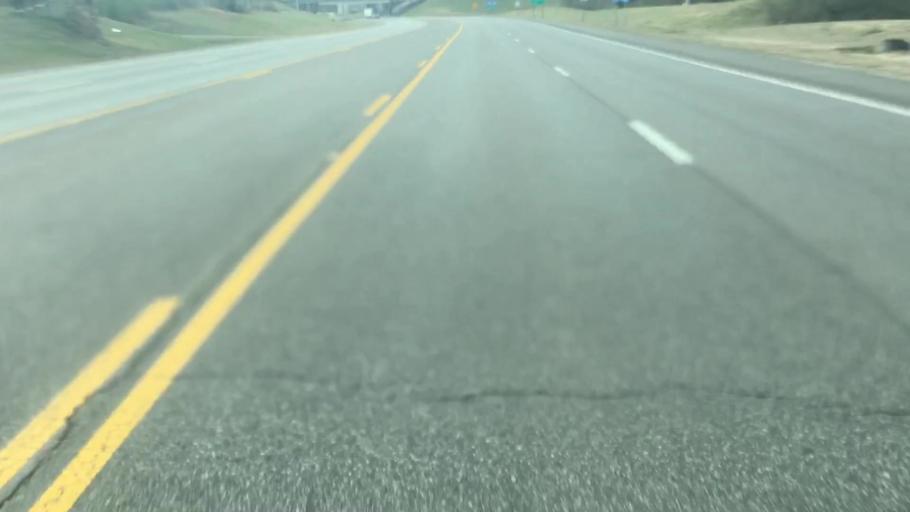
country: US
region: Alabama
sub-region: Walker County
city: Jasper
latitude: 33.7974
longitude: -87.2383
